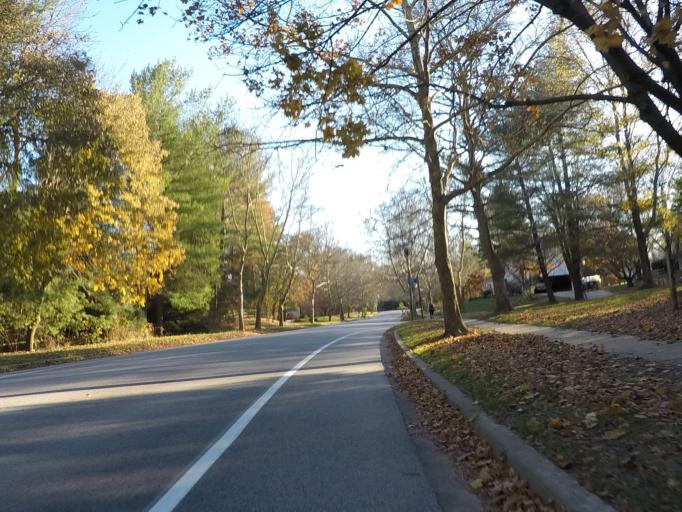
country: US
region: Maryland
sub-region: Howard County
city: Columbia
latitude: 39.2560
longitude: -76.8391
